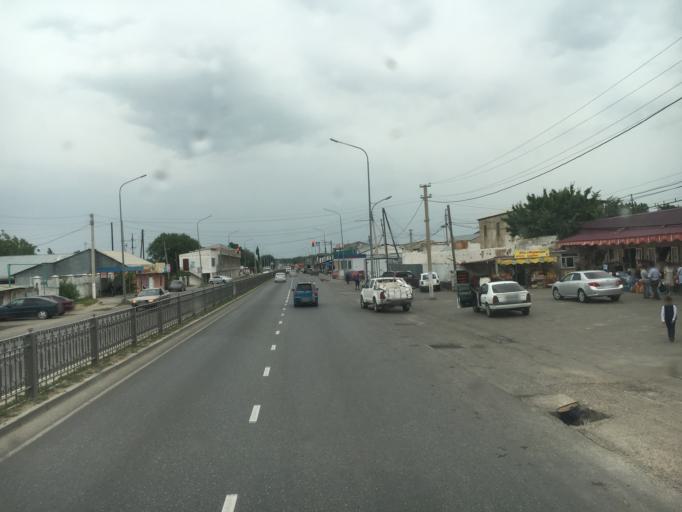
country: KZ
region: Ongtustik Qazaqstan
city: Shymkent
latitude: 42.3731
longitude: 69.5036
